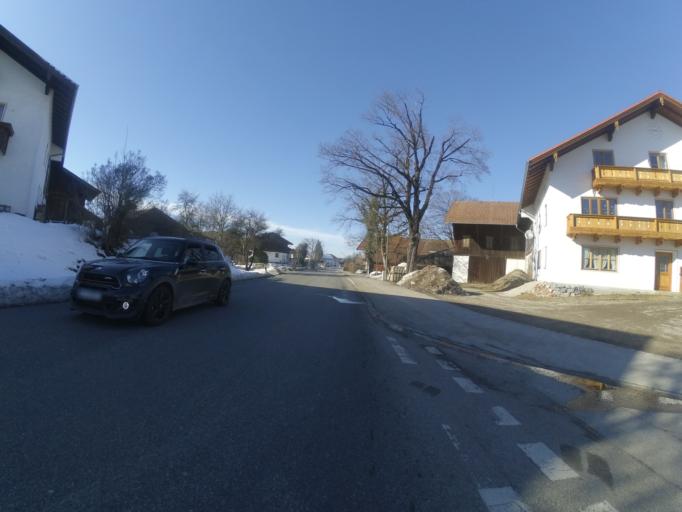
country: DE
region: Bavaria
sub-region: Upper Bavaria
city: Aying
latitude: 47.9514
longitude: 11.7884
